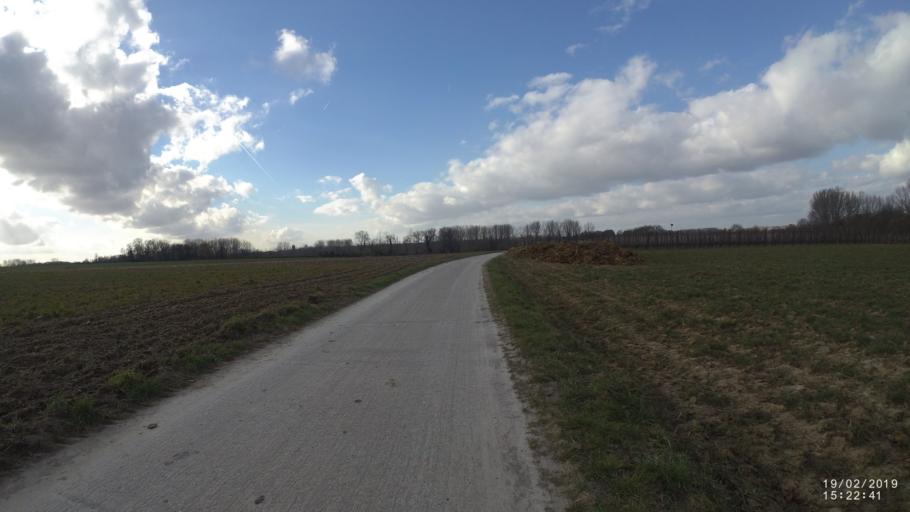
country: BE
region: Flanders
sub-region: Provincie Limburg
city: Tongeren
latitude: 50.7947
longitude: 5.4142
